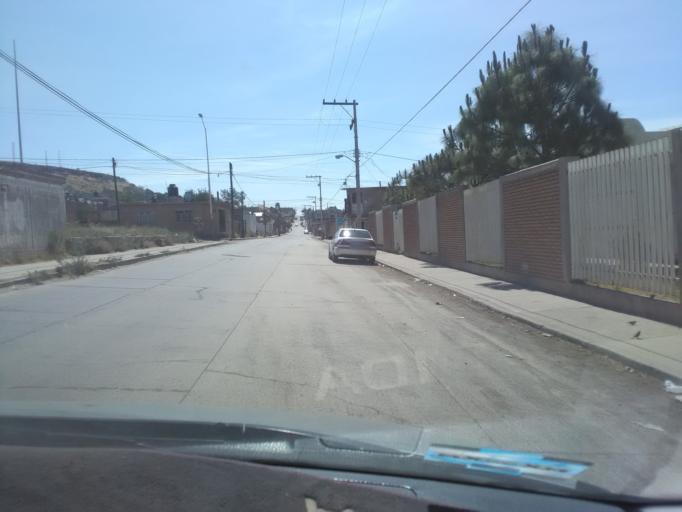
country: MX
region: Durango
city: Victoria de Durango
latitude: 24.0303
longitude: -104.7083
